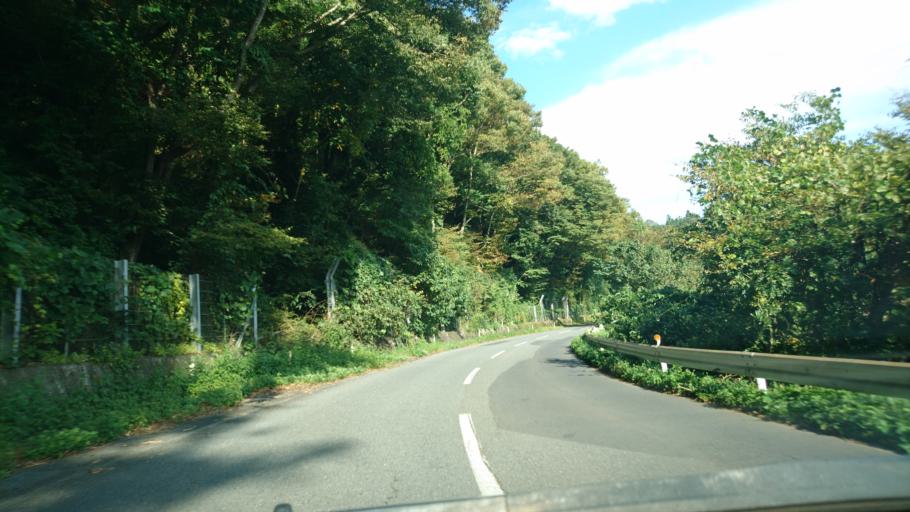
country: JP
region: Iwate
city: Ichinoseki
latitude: 38.8575
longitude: 141.3103
